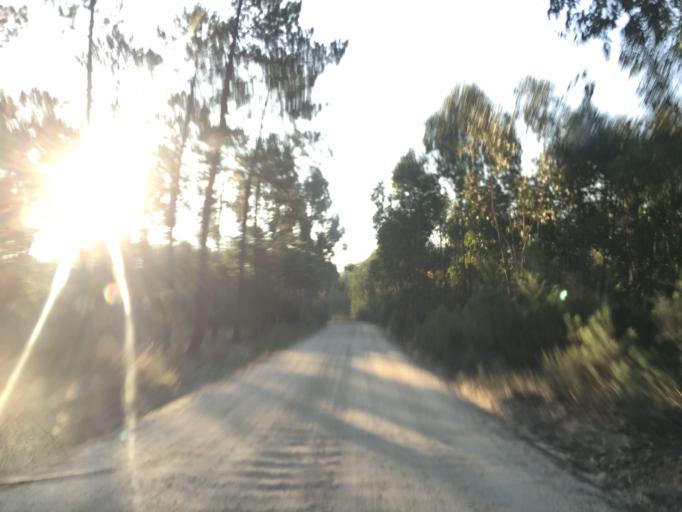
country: PT
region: Portalegre
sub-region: Ponte de Sor
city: Santo Andre
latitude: 39.0921
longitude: -8.3759
